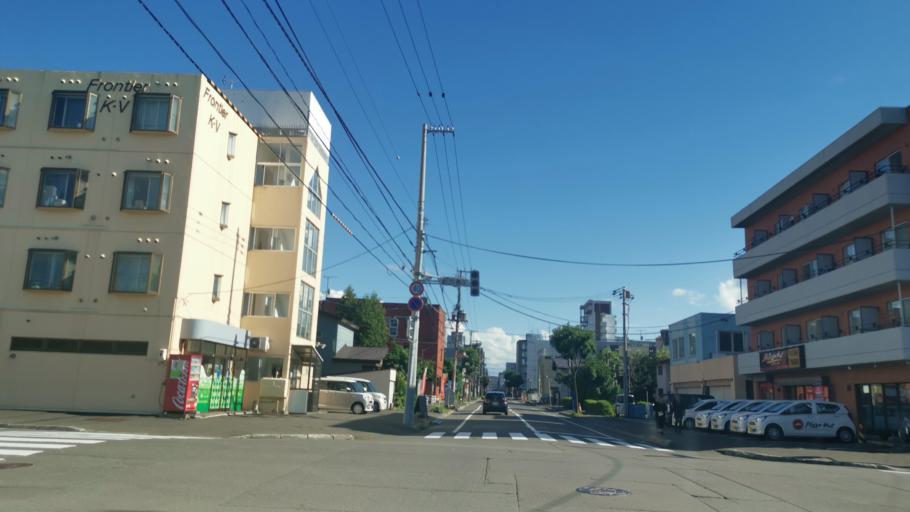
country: JP
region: Hokkaido
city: Sapporo
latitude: 43.0854
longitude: 141.3458
